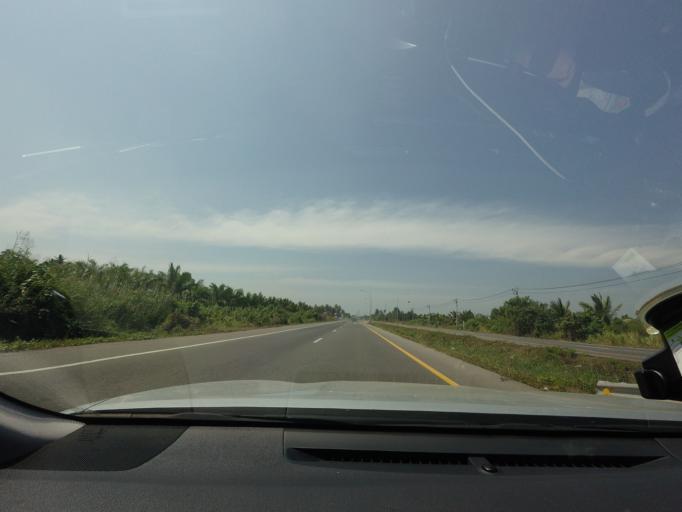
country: TH
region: Surat Thani
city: Surat Thani
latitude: 9.1733
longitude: 99.2972
